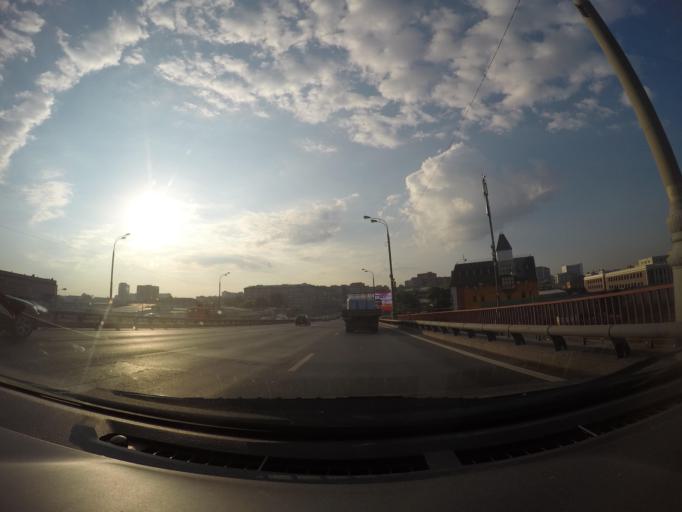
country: RU
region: Moscow
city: Sokol'niki
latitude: 55.7786
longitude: 37.6760
